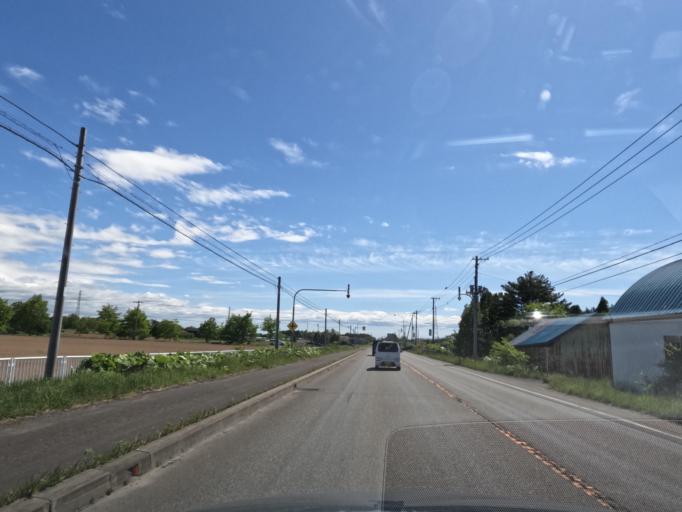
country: JP
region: Hokkaido
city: Kitahiroshima
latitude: 43.0226
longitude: 141.7088
